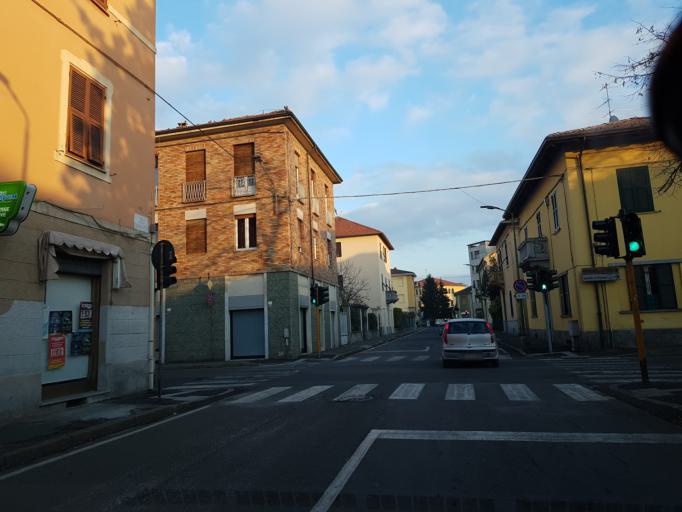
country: IT
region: Piedmont
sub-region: Provincia di Alessandria
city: Novi Ligure
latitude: 44.7639
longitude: 8.7964
